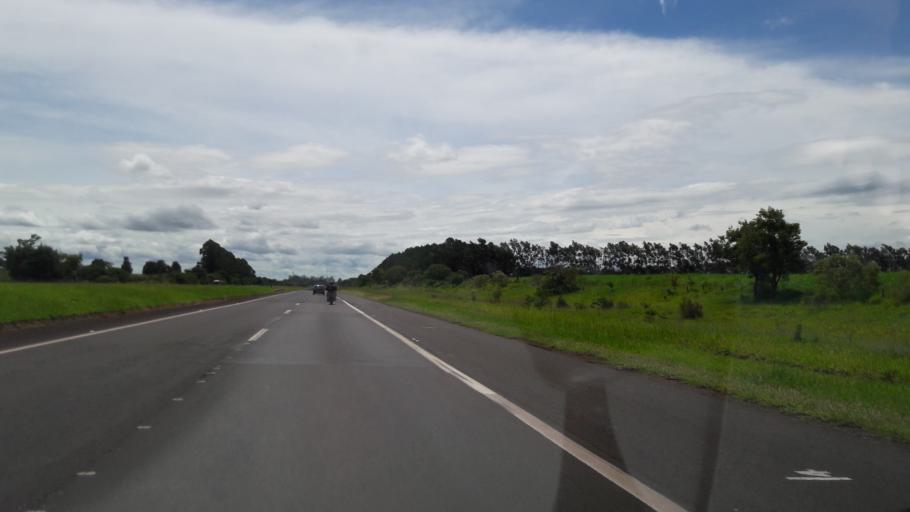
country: BR
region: Sao Paulo
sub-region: Avare
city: Avare
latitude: -22.9406
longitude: -48.9326
